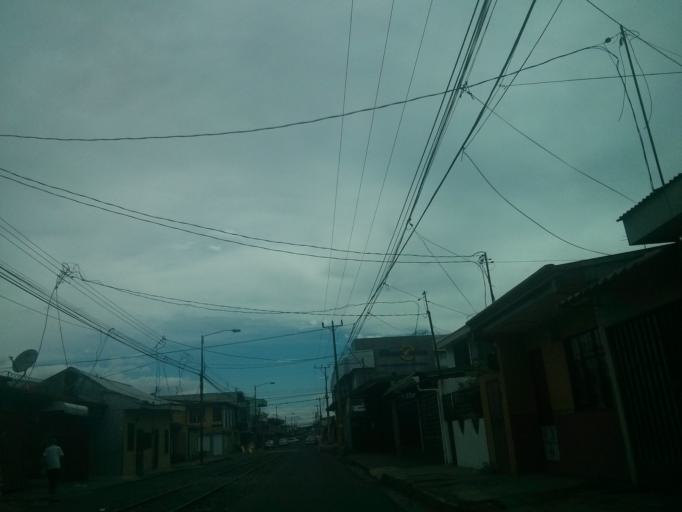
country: CR
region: Heredia
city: Heredia
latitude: 9.9950
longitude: -84.1195
